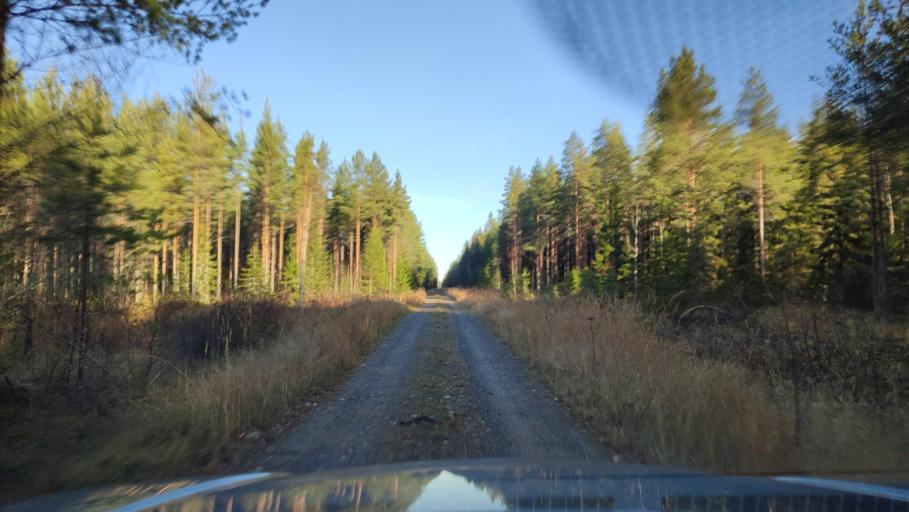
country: FI
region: Southern Ostrobothnia
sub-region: Suupohja
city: Karijoki
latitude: 62.1827
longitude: 21.6085
